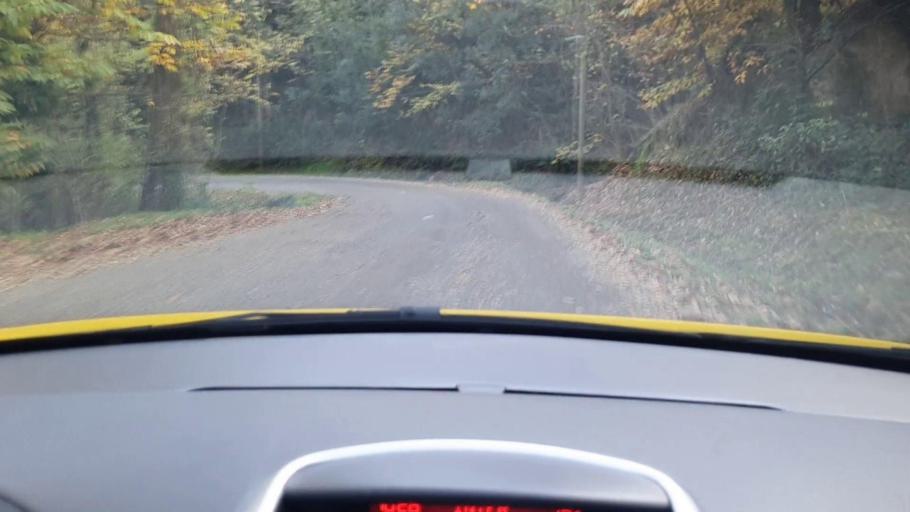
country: FR
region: Languedoc-Roussillon
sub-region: Departement du Gard
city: Lasalle
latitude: 44.0289
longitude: 3.8347
